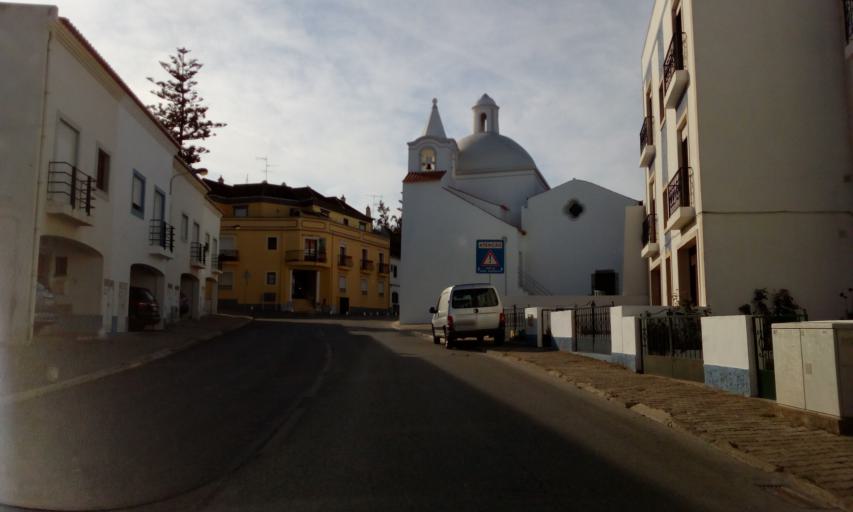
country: PT
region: Faro
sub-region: Tavira
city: Tavira
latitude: 37.1258
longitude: -7.6540
